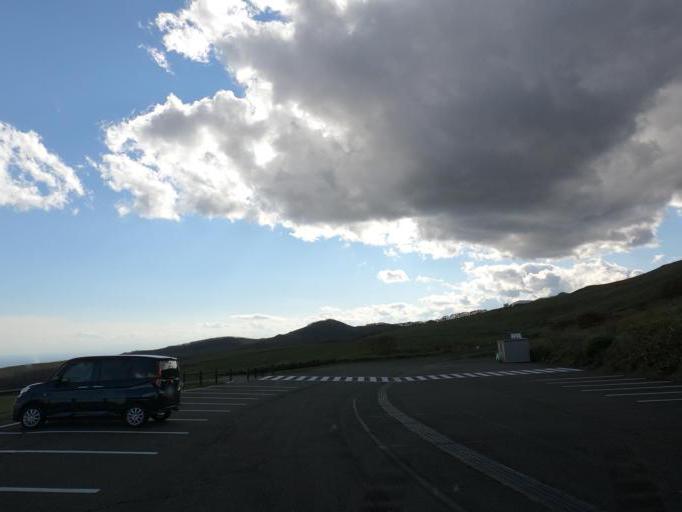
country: JP
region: Hokkaido
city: Otofuke
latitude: 43.2861
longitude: 143.1841
